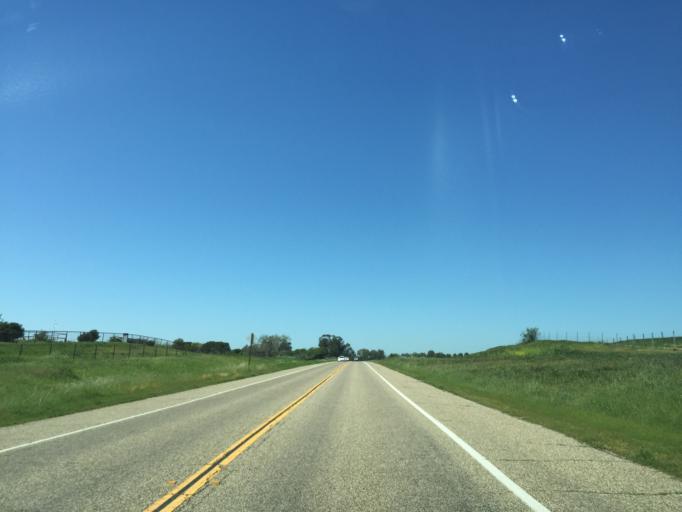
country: US
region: California
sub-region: Santa Barbara County
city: Santa Ynez
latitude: 34.6245
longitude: -120.0716
